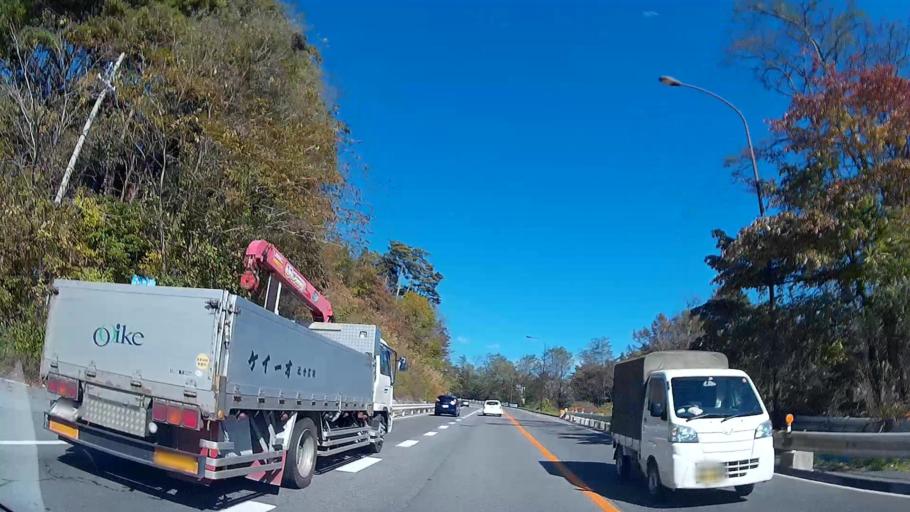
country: JP
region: Nagano
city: Okaya
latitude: 36.0803
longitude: 138.0323
